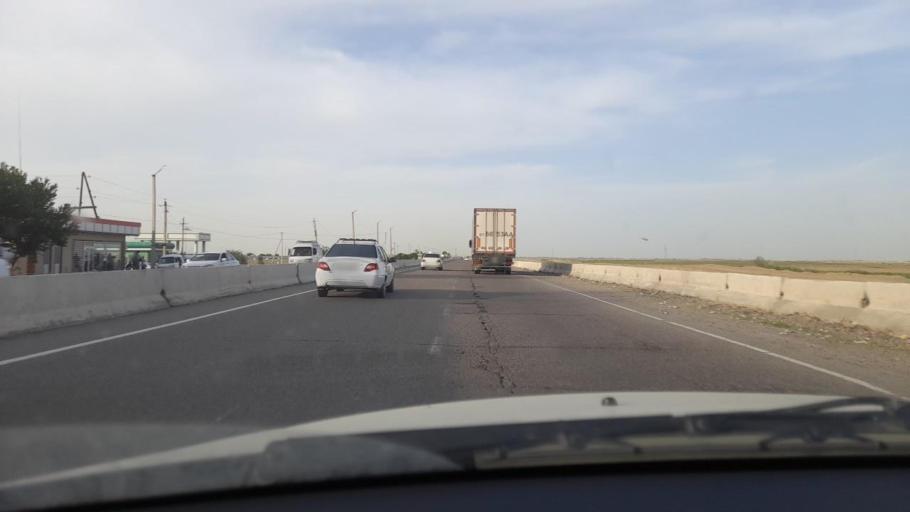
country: UZ
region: Jizzax
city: Gagarin
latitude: 40.4504
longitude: 68.2490
